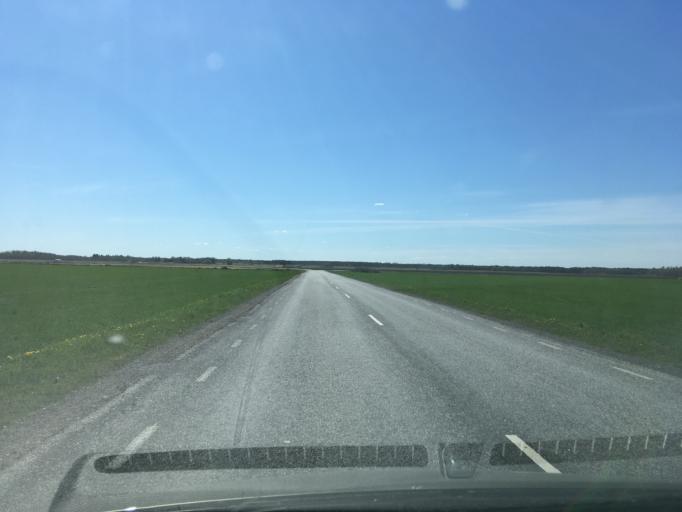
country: EE
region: Harju
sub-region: Raasiku vald
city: Arukula
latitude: 59.4287
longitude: 25.0796
